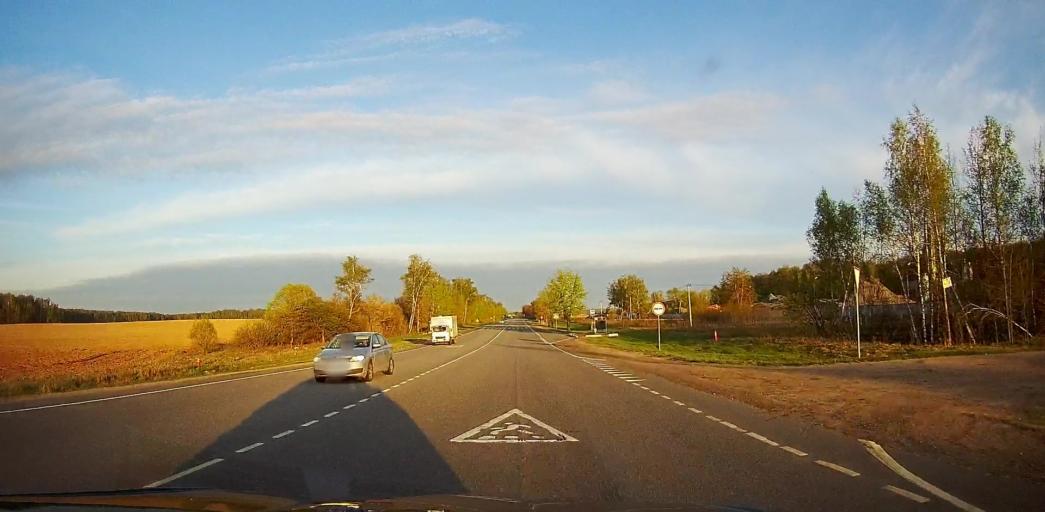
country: RU
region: Moskovskaya
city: Troitskoye
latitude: 55.2162
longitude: 38.5916
